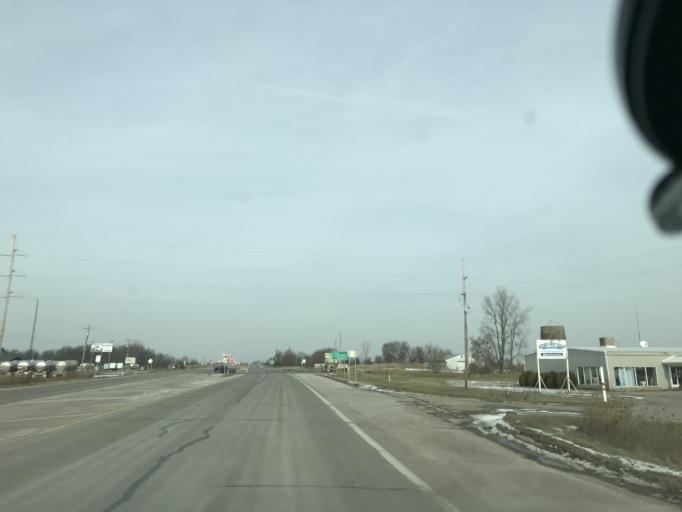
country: US
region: Michigan
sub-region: Ionia County
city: Lake Odessa
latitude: 42.8734
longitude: -85.0749
